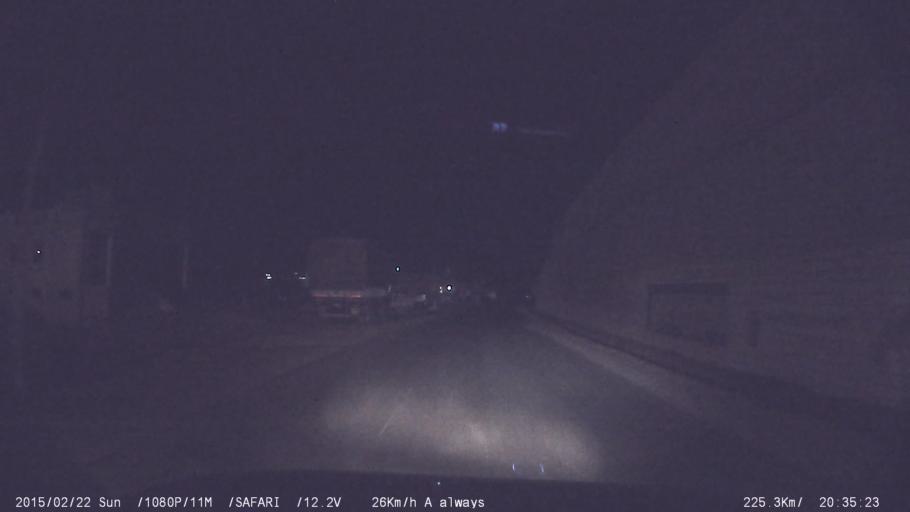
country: IN
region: Tamil Nadu
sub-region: Dindigul
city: Dindigul
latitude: 10.3728
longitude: 77.9519
